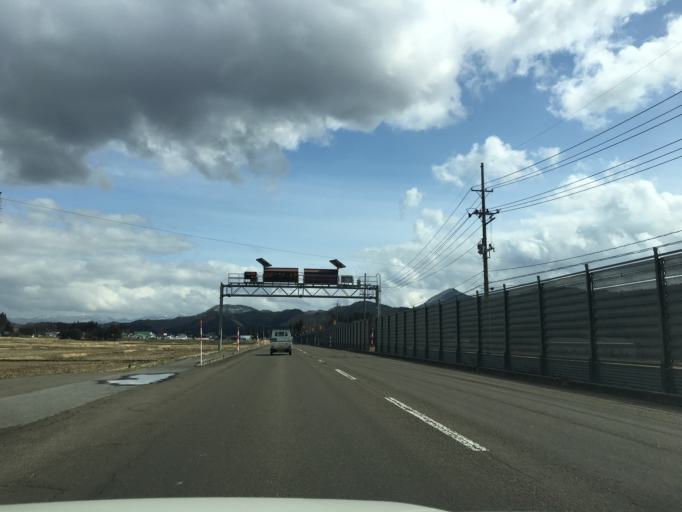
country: JP
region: Akita
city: Odate
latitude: 40.2172
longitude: 140.6165
